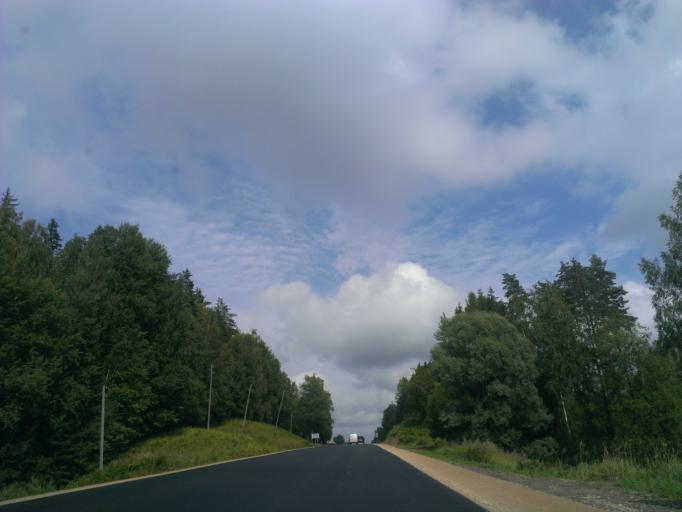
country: LV
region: Amatas Novads
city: Drabesi
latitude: 57.2246
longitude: 25.2446
